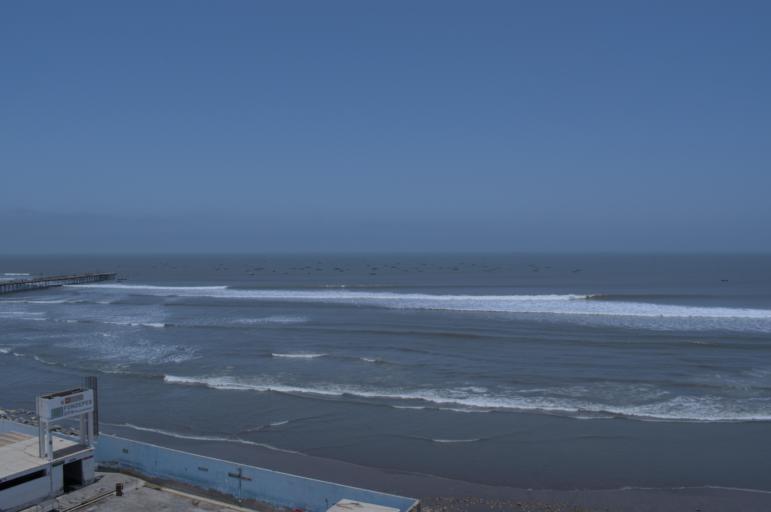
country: PE
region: La Libertad
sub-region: Provincia de Pacasmayo
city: Pacasmayo
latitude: -7.3970
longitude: -79.5704
